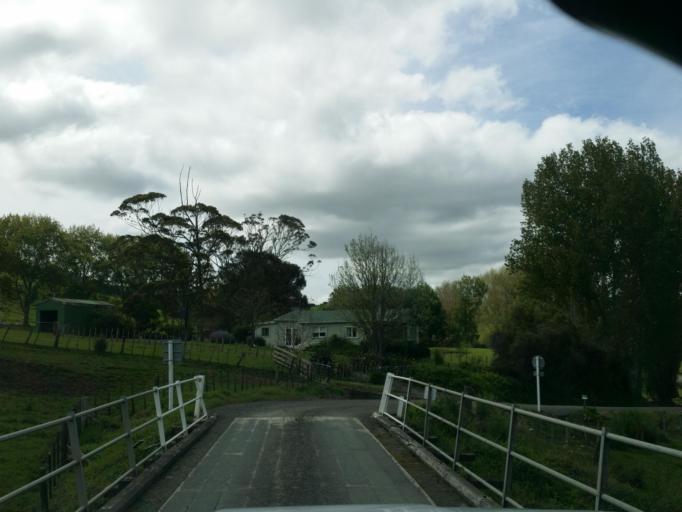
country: NZ
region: Northland
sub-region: Kaipara District
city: Dargaville
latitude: -35.8783
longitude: 174.0424
